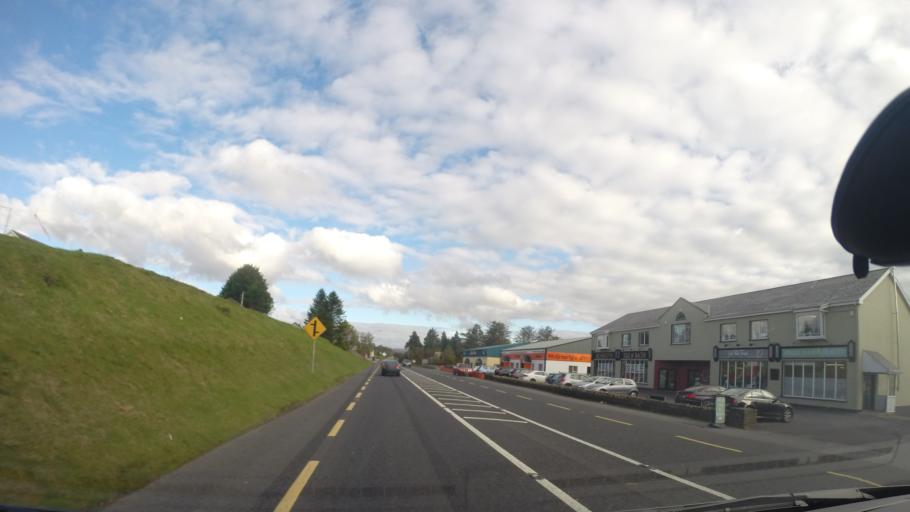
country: IE
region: Ulster
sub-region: County Donegal
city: Donegal
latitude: 54.6523
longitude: -8.1449
